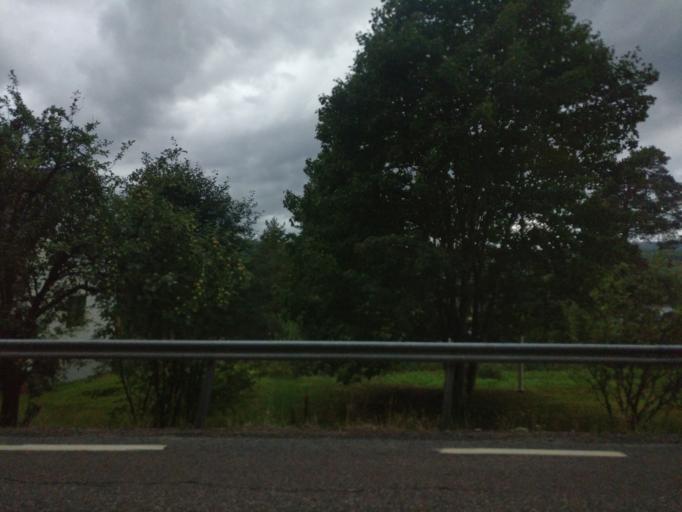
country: SE
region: Vaermland
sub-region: Torsby Kommun
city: Torsby
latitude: 60.6231
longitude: 13.0322
